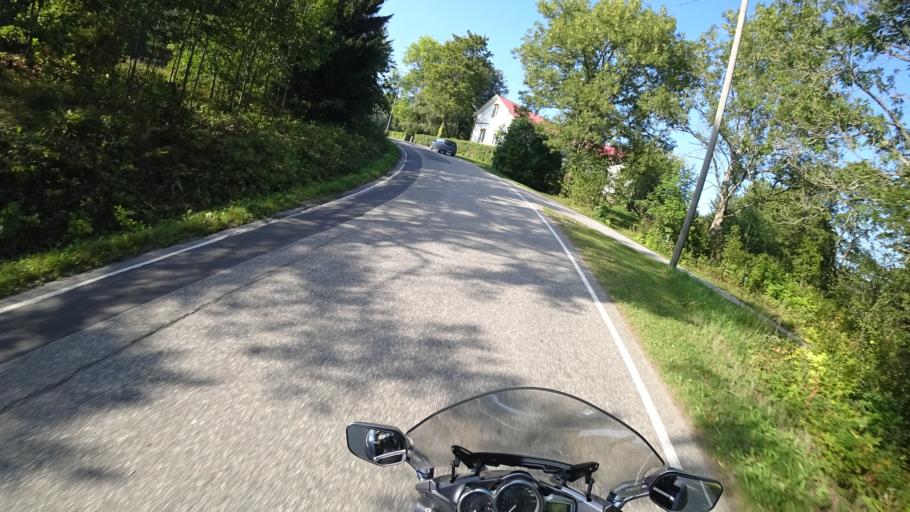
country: FI
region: Varsinais-Suomi
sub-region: Salo
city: Suomusjaervi
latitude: 60.3558
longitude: 23.6502
